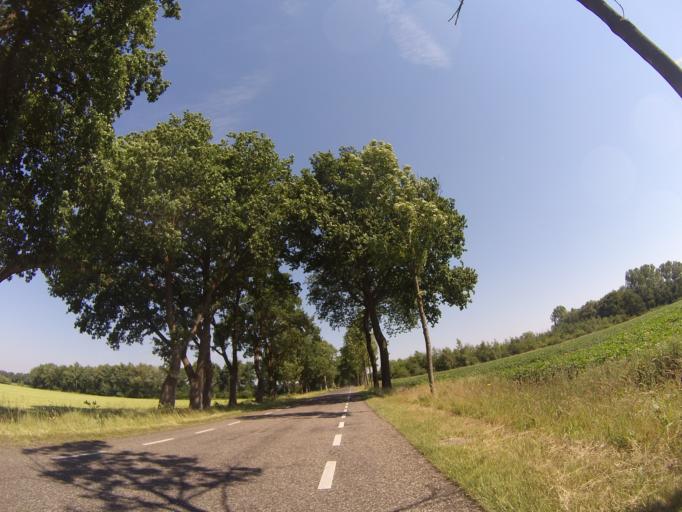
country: NL
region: Drenthe
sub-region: Gemeente Coevorden
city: Sleen
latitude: 52.8124
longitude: 6.7405
